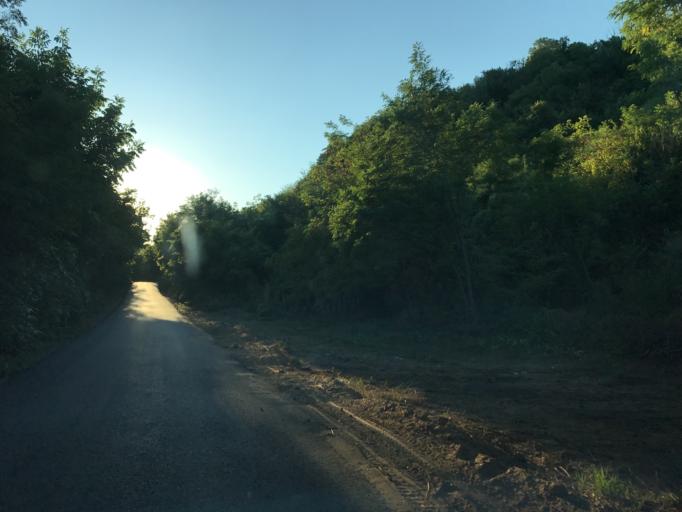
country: BG
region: Vidin
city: Bregovo
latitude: 44.1201
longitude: 22.5884
